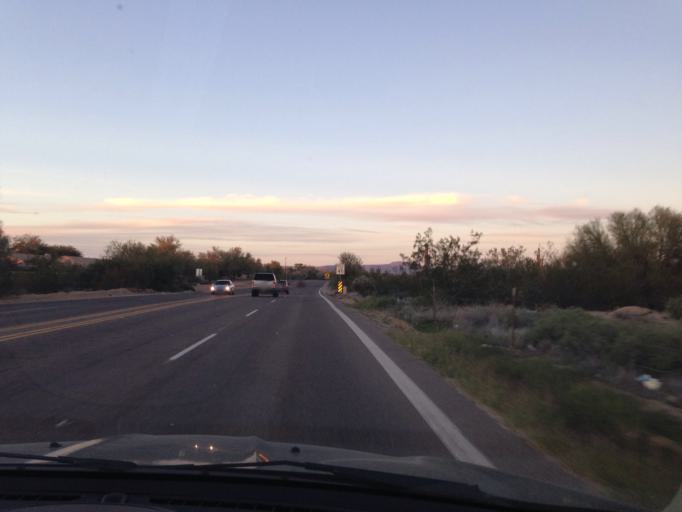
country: US
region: Arizona
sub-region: Maricopa County
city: Cave Creek
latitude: 33.7312
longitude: -111.9777
